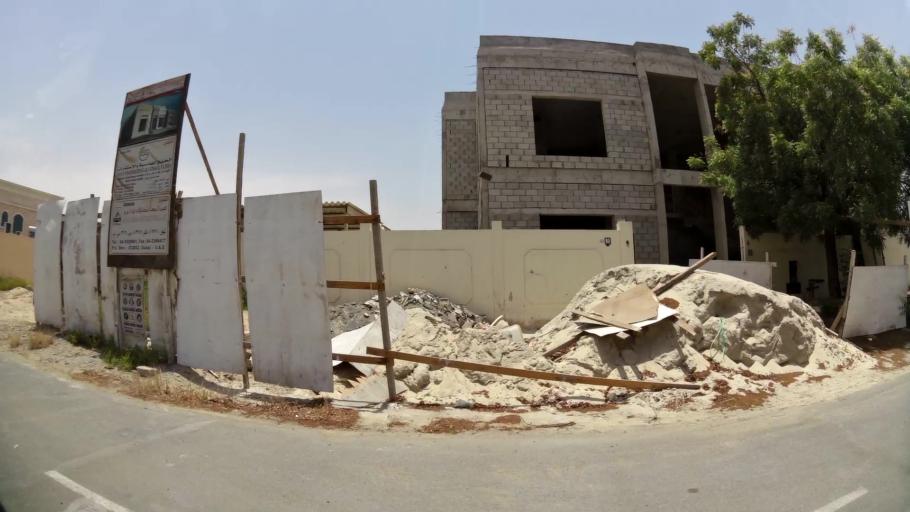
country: AE
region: Ash Shariqah
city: Sharjah
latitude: 25.2103
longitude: 55.3951
